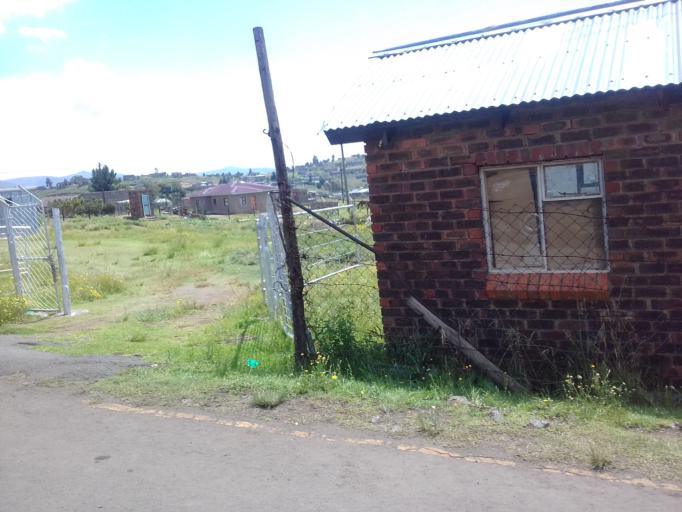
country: LS
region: Thaba-Tseka
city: Thaba-Tseka
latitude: -29.5197
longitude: 28.6096
